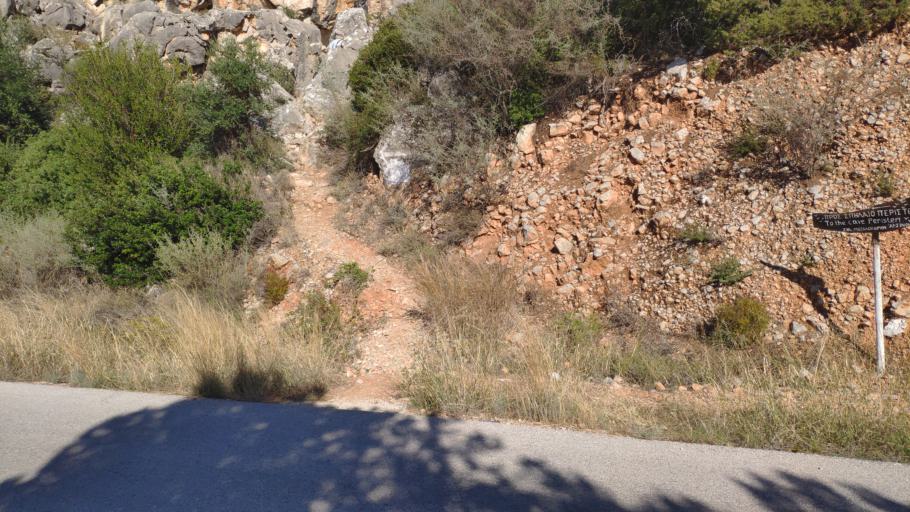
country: GR
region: Attica
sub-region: Nomos Piraios
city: Galatas
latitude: 37.5732
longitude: 23.3598
